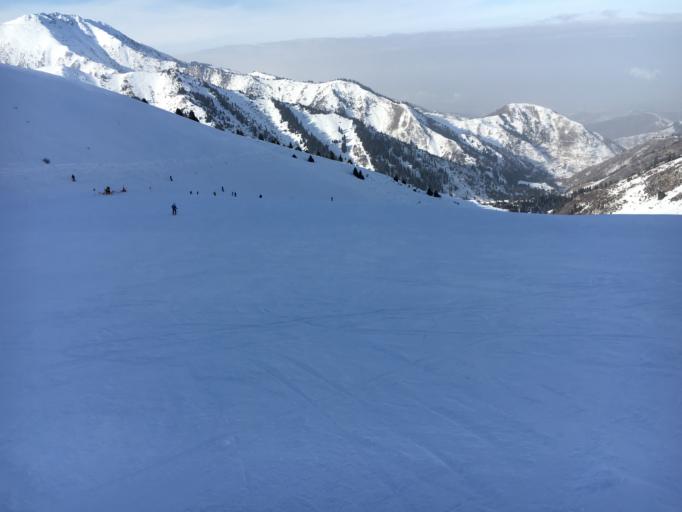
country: KZ
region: Almaty Qalasy
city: Almaty
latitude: 43.1187
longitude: 77.0987
